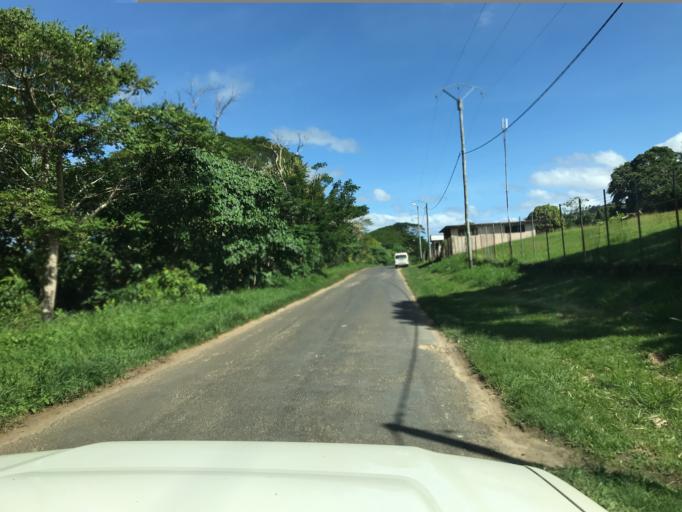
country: VU
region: Sanma
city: Luganville
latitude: -15.5357
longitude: 167.1542
